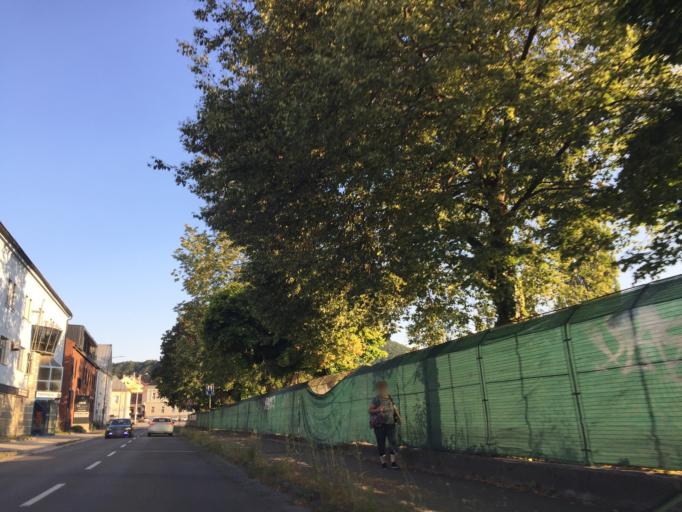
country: SK
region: Banskobystricky
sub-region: Okres Banska Bystrica
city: Banska Bystrica
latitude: 48.7387
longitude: 19.1415
